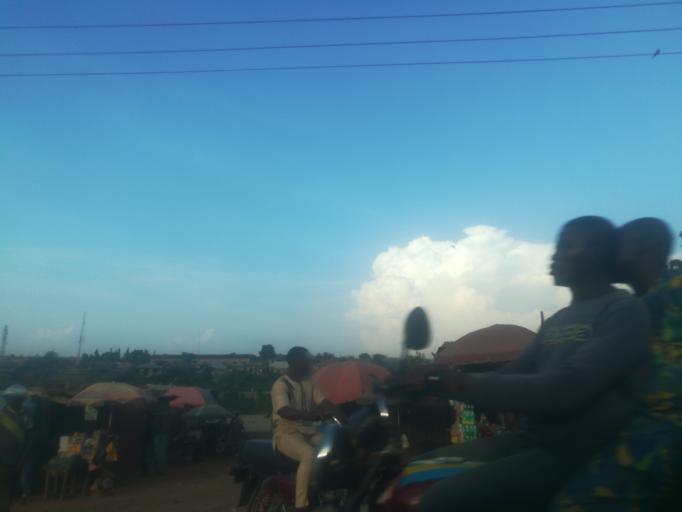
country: NG
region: Oyo
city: Moniya
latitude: 7.5334
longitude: 3.9078
